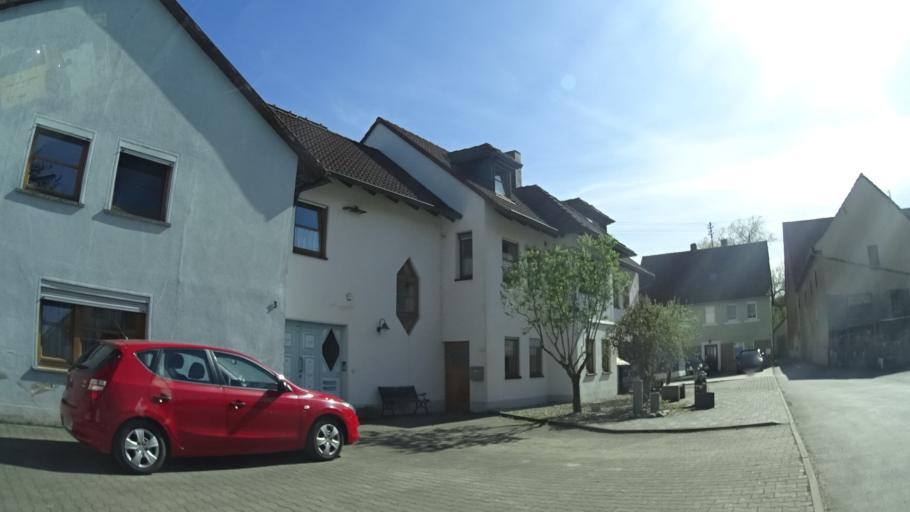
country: DE
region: Bavaria
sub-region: Regierungsbezirk Unterfranken
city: Burgpreppach
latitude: 50.1221
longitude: 10.6335
